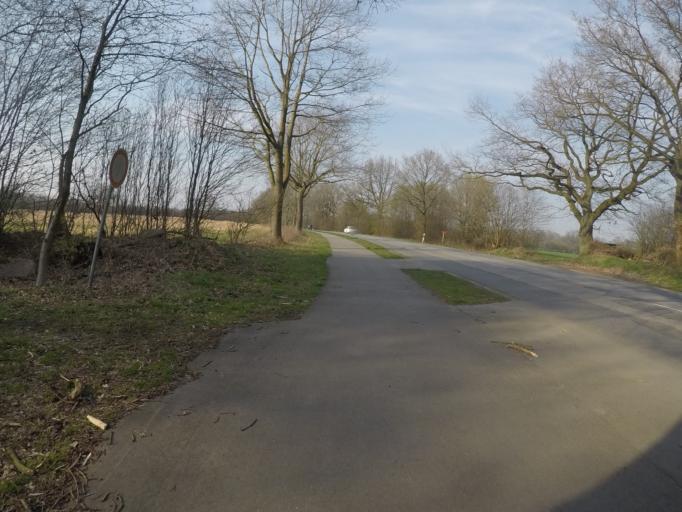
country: DE
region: Schleswig-Holstein
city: Wittenborn
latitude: 53.9328
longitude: 10.2253
